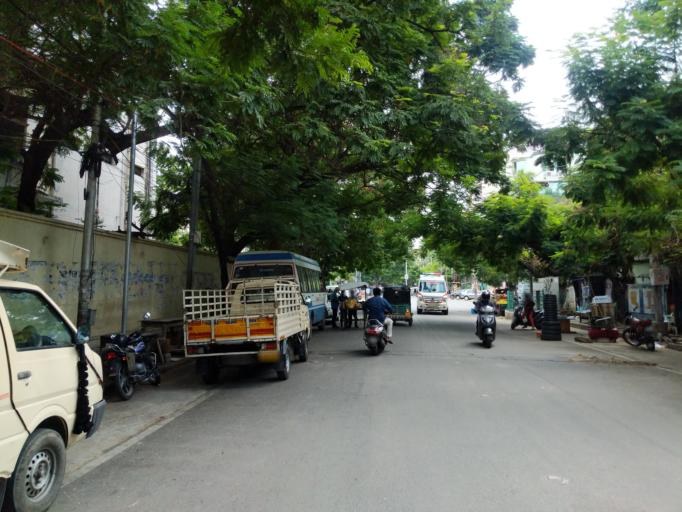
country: IN
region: Telangana
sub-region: Hyderabad
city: Hyderabad
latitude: 17.4384
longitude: 78.4512
